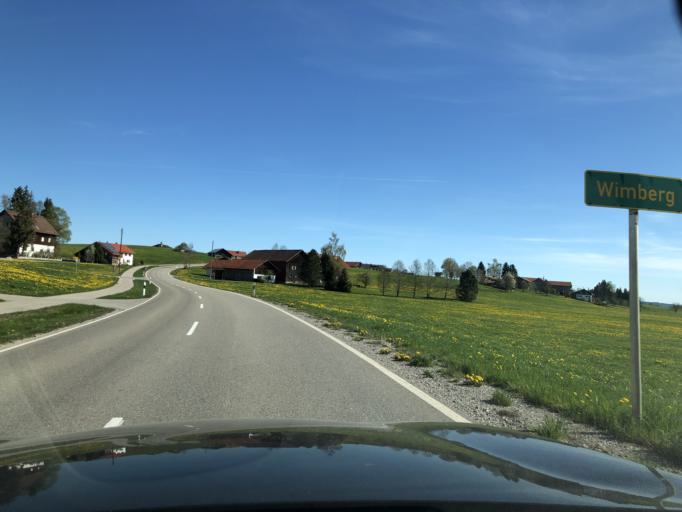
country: DE
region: Bavaria
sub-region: Swabia
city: Wald
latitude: 47.6973
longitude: 10.5459
